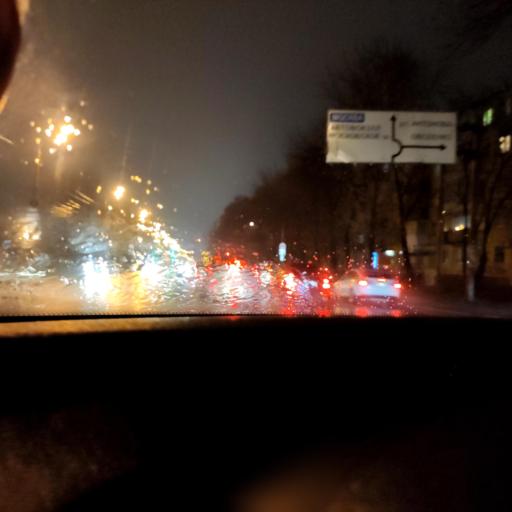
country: RU
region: Samara
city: Samara
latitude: 53.2082
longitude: 50.1896
